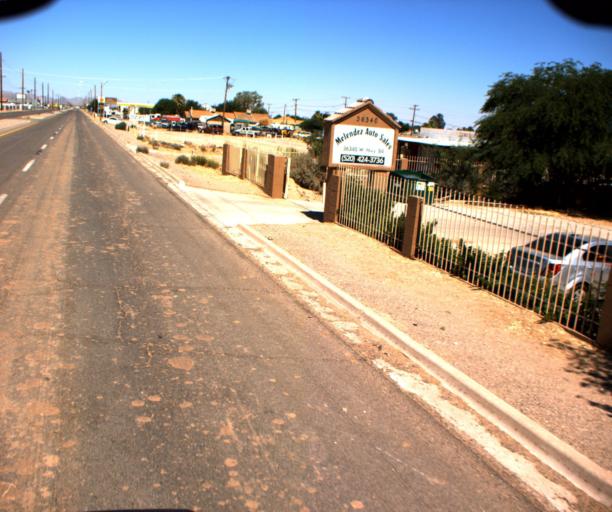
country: US
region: Arizona
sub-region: Pinal County
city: Maricopa
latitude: 32.8795
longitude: -111.9582
